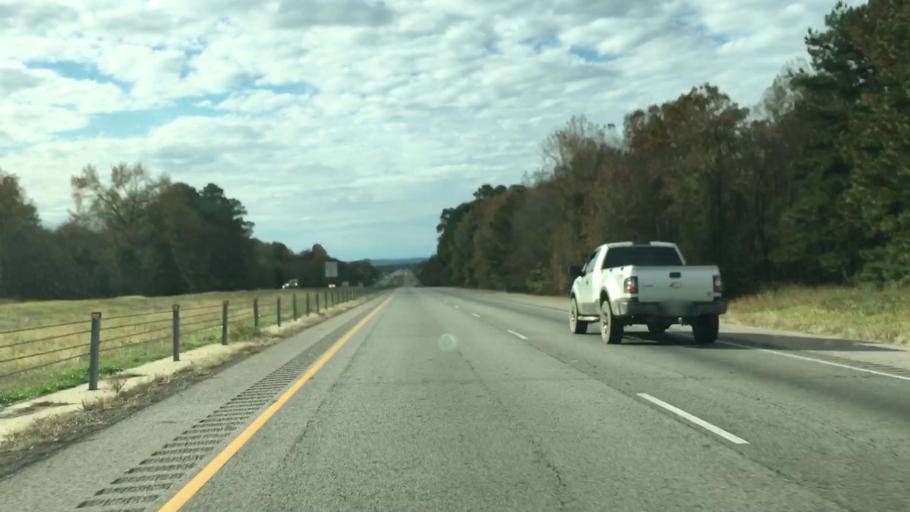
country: US
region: Arkansas
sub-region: Conway County
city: Morrilton
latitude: 35.1800
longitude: -92.7577
